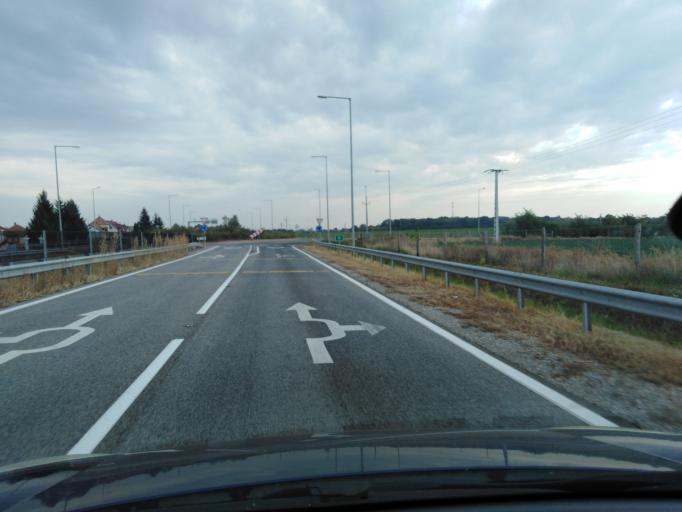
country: HU
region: Heves
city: Zagyvaszanto
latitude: 47.7729
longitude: 19.6609
